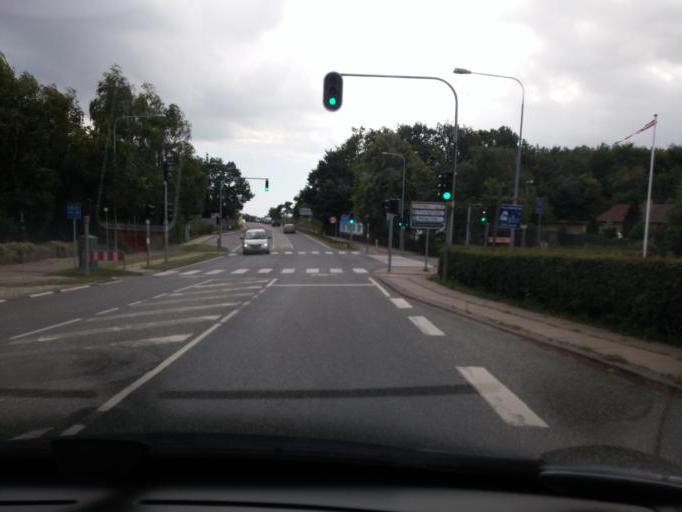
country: DK
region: South Denmark
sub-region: Svendborg Kommune
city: Vindeby
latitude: 55.0219
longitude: 10.6075
